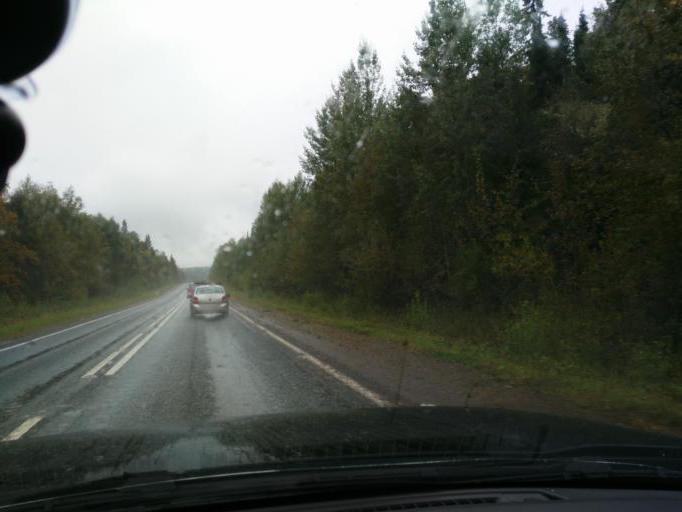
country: RU
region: Perm
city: Yugo-Kamskiy
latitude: 57.6094
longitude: 55.6444
